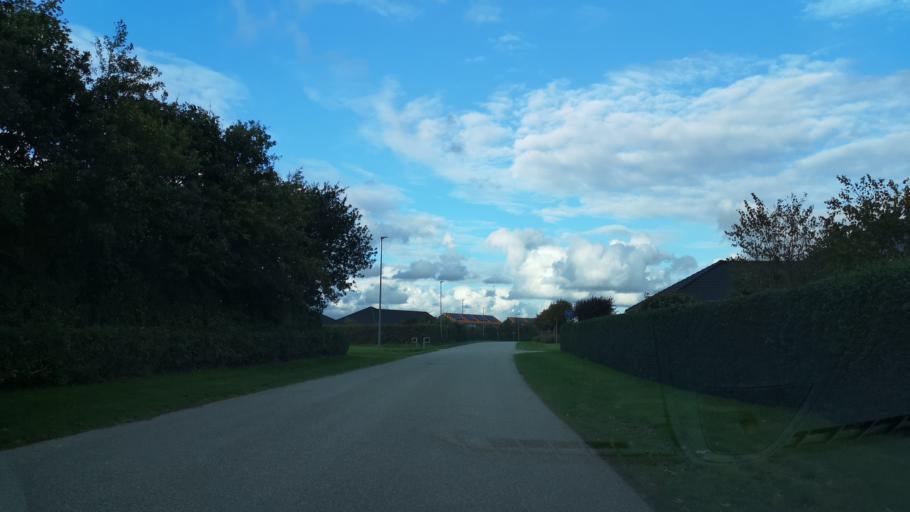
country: DK
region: Central Jutland
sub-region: Ringkobing-Skjern Kommune
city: Ringkobing
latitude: 56.0920
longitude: 8.2733
